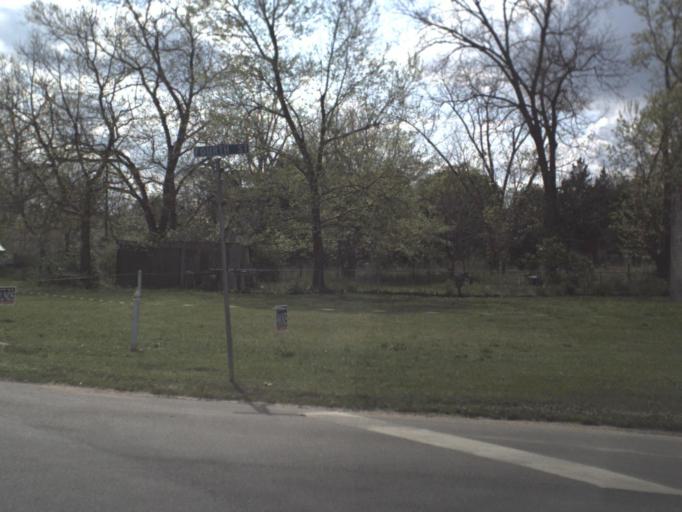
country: US
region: Alabama
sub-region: Covington County
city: Florala
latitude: 30.9655
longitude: -86.4615
